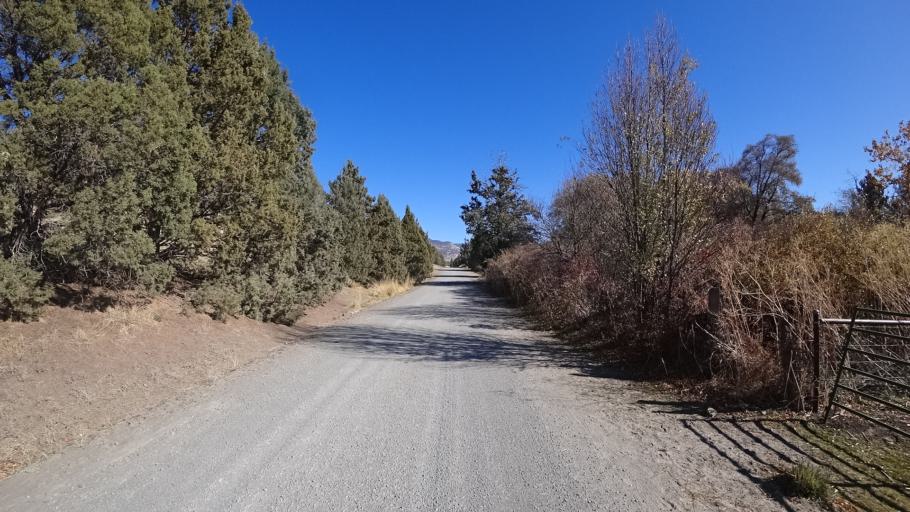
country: US
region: California
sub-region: Siskiyou County
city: Montague
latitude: 41.7319
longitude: -122.3537
